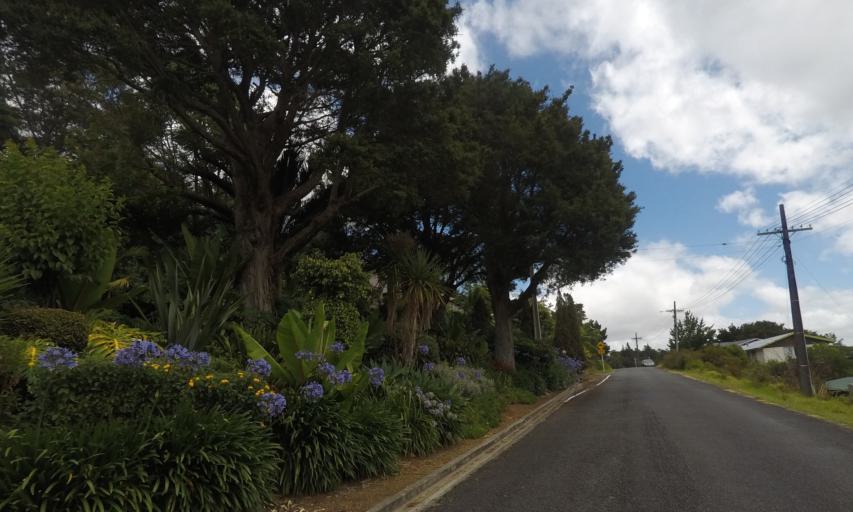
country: NZ
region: Northland
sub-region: Whangarei
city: Whangarei
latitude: -35.7429
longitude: 174.3611
